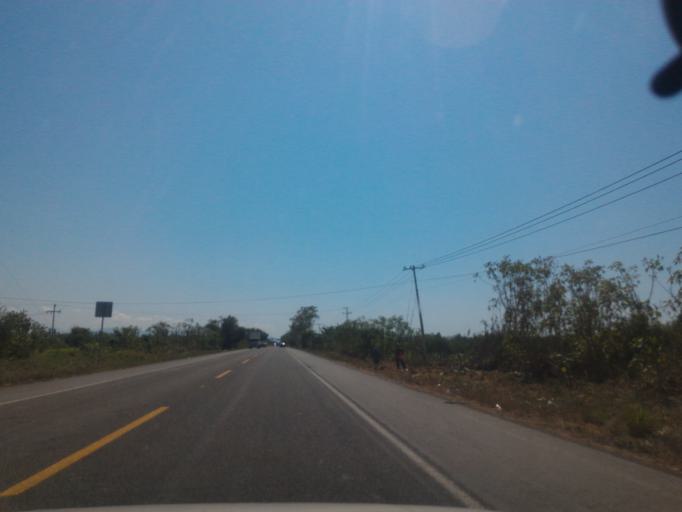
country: MX
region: Colima
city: Tecoman
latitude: 18.8267
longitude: -103.8135
